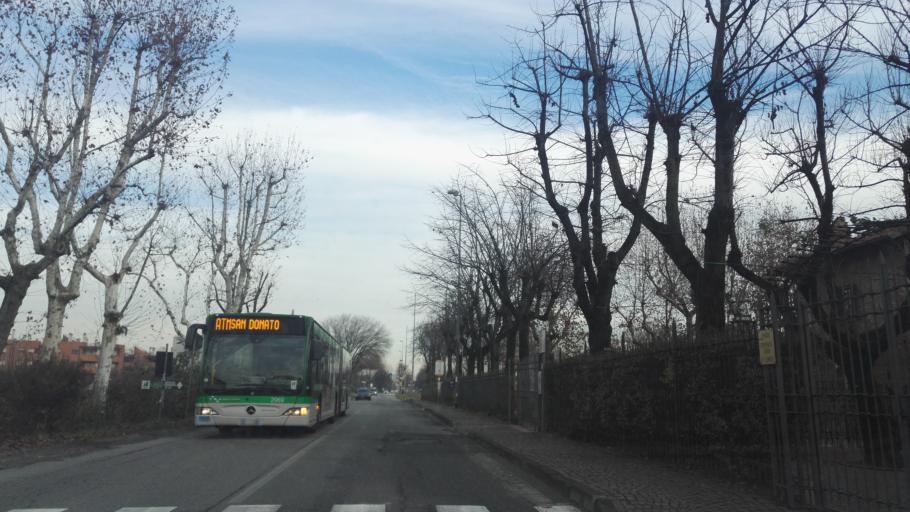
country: IT
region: Lombardy
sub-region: Citta metropolitana di Milano
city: San Bovio-San Felice
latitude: 45.4627
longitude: 9.3034
